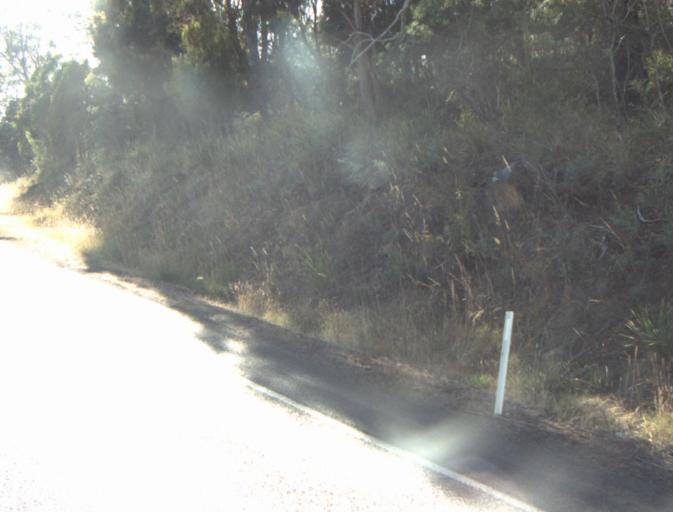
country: AU
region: Tasmania
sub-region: Launceston
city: Newstead
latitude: -41.4192
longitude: 147.2765
